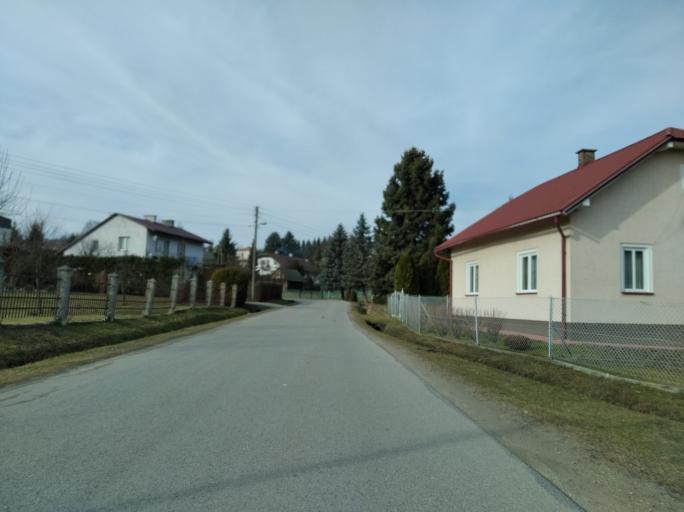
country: PL
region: Subcarpathian Voivodeship
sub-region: Powiat brzozowski
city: Turze Pole
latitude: 49.6662
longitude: 22.0040
